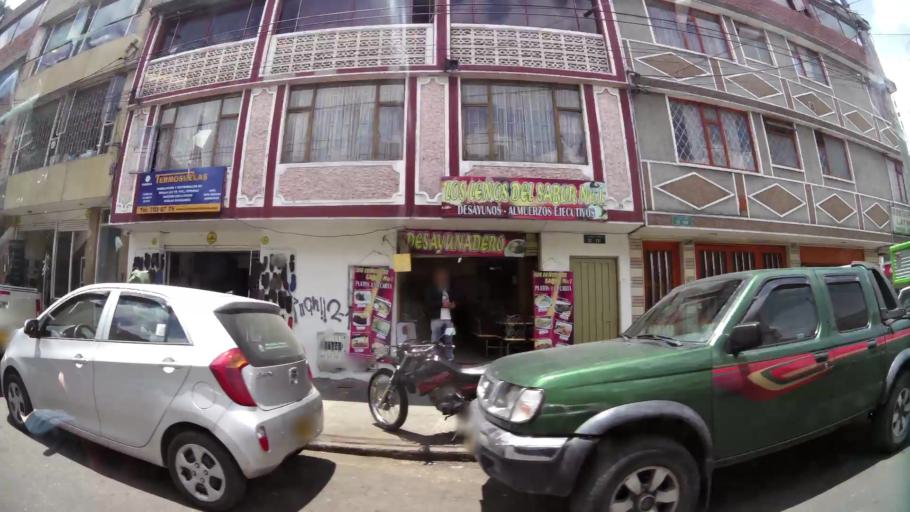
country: CO
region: Bogota D.C.
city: Bogota
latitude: 4.5889
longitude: -74.1042
